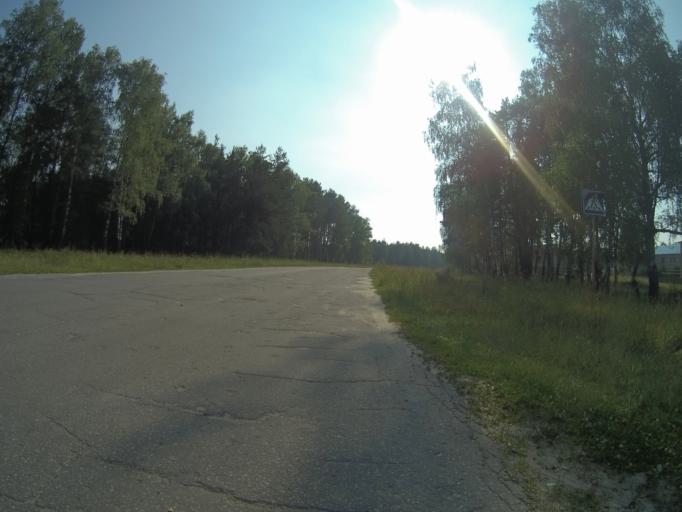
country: RU
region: Vladimir
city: Andreyevo
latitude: 55.9412
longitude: 41.0729
